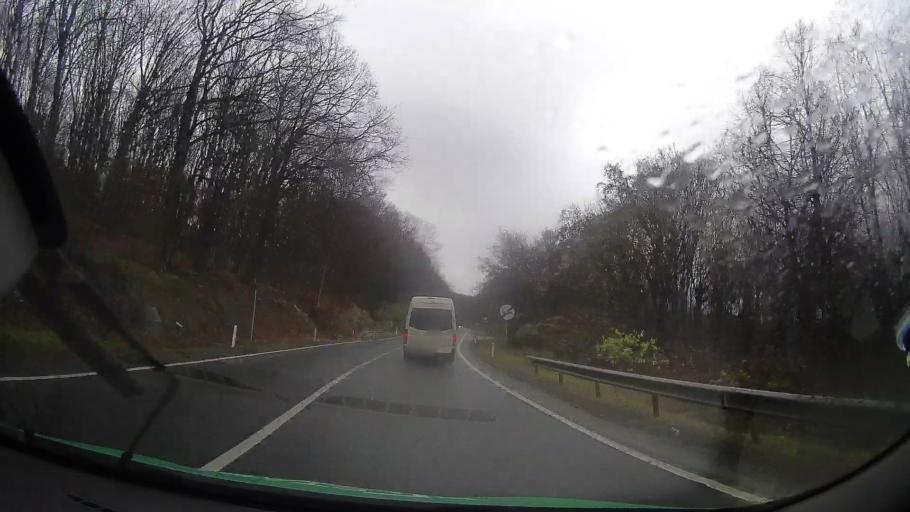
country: RO
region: Bistrita-Nasaud
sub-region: Comuna Sieu-Magherus
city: Sieu-Magherus
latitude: 47.0384
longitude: 24.4208
